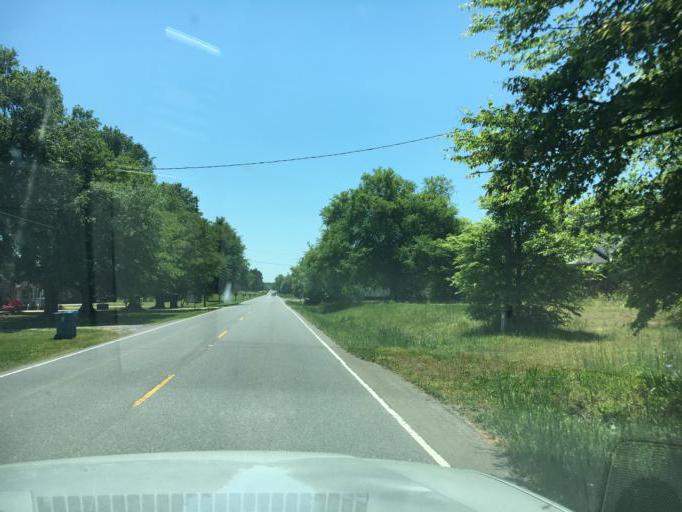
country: US
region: South Carolina
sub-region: Cherokee County
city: Blacksburg
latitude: 35.1970
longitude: -81.5642
